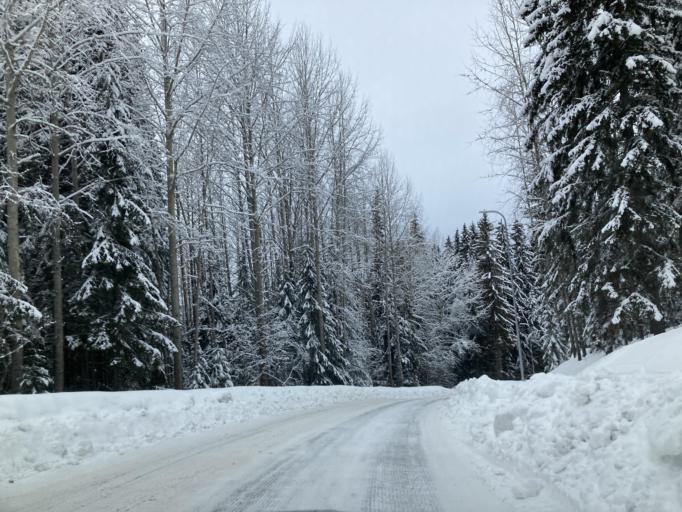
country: FI
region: Central Finland
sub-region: Jaemsae
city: Jaemsae
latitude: 61.8782
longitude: 25.3074
